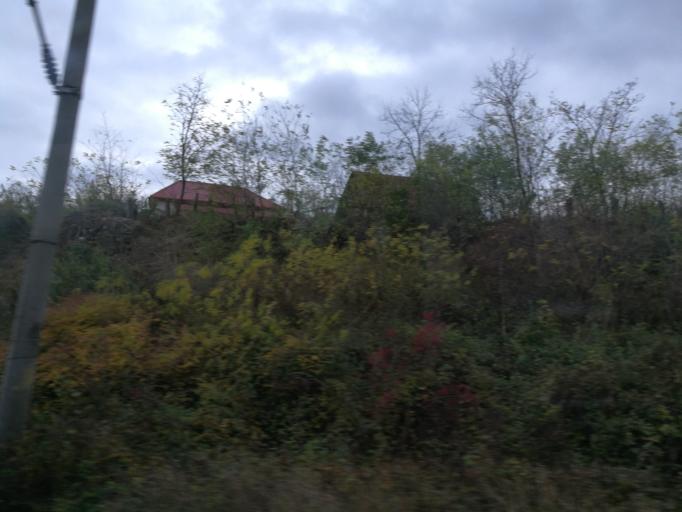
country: RO
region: Iasi
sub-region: Comuna Stolniceni-Prajescu
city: Stolniceni-Prajescu
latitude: 47.2046
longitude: 26.7419
